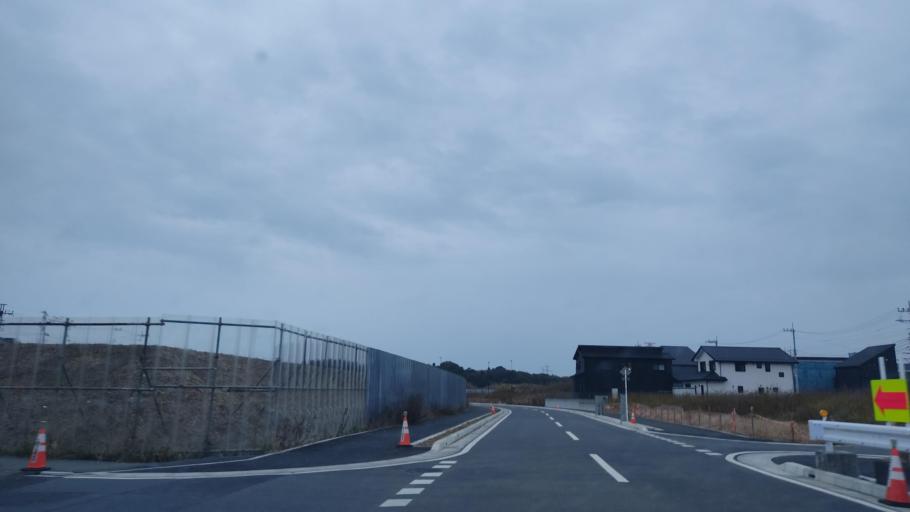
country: JP
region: Chiba
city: Kashiwa
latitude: 35.9034
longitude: 139.9564
